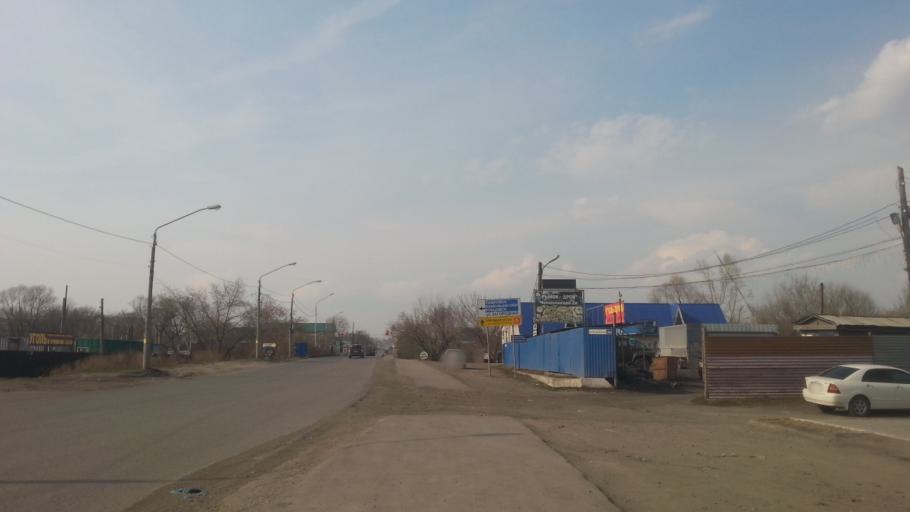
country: RU
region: Altai Krai
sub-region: Gorod Barnaulskiy
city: Barnaul
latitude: 53.3217
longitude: 83.7690
